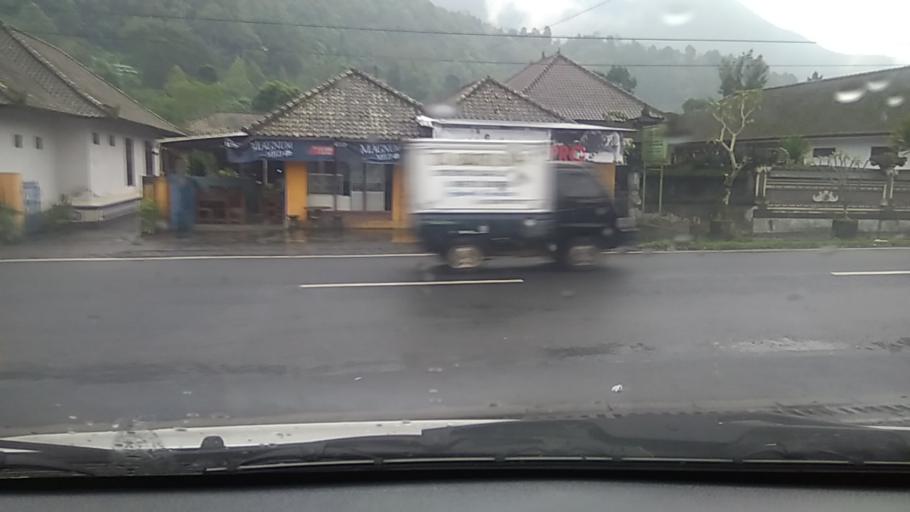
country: ID
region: Bali
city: Munduk
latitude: -8.2577
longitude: 115.1619
